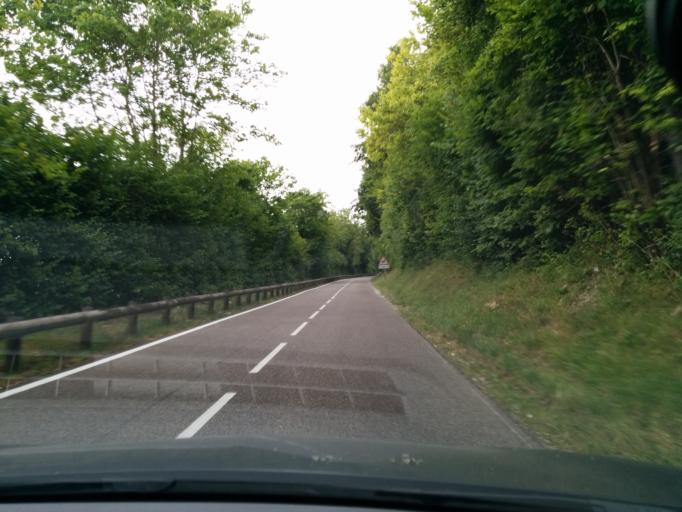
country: FR
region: Ile-de-France
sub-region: Departement des Yvelines
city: Limetz-Villez
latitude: 49.0659
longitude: 1.5204
